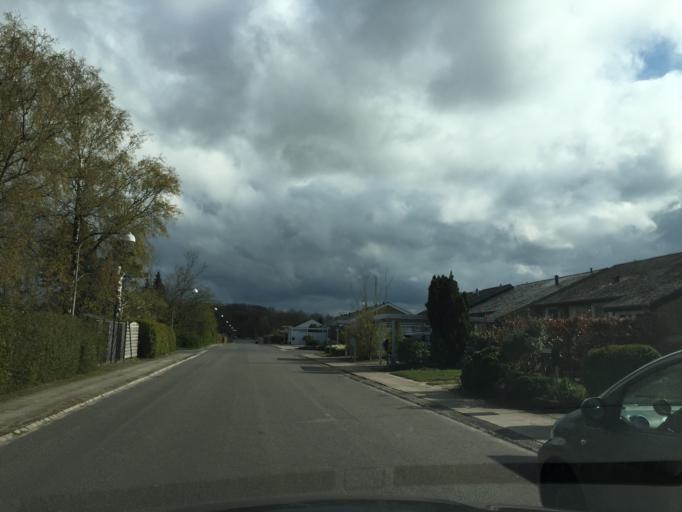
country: DK
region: South Denmark
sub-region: Odense Kommune
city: Neder Holluf
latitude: 55.3769
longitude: 10.4184
